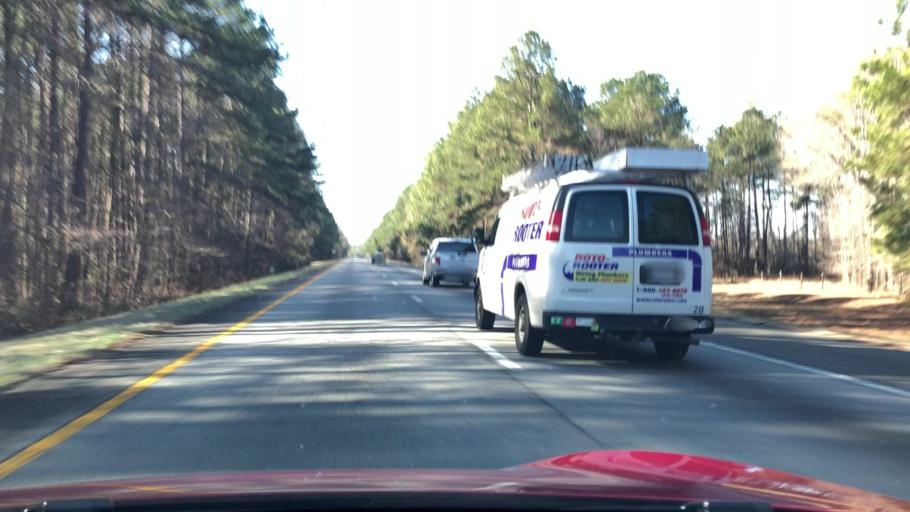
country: US
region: South Carolina
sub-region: Clarendon County
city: Manning
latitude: 33.5630
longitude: -80.3944
